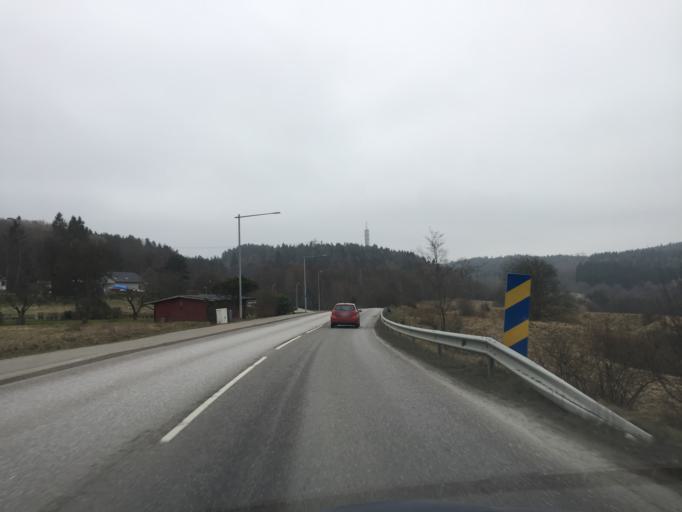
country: SE
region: Vaestra Goetaland
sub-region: Goteborg
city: Rannebergen
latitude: 57.7767
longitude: 12.0733
